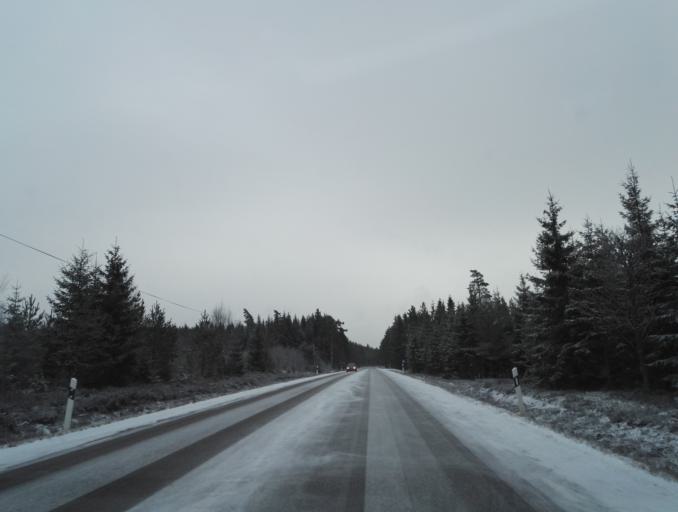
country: SE
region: Kronoberg
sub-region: Uppvidinge Kommun
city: Lenhovda
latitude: 56.9810
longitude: 15.2985
